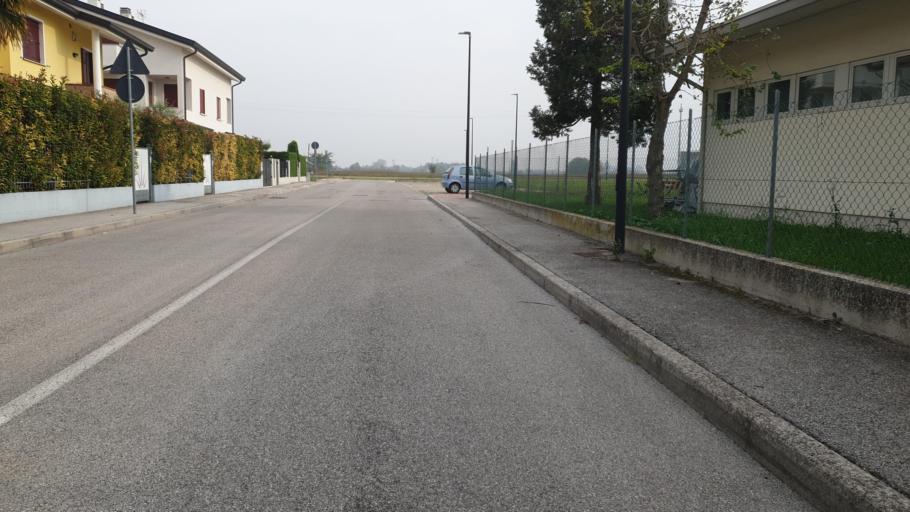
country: IT
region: Veneto
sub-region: Provincia di Padova
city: Casalserugo
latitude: 45.2970
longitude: 11.9090
